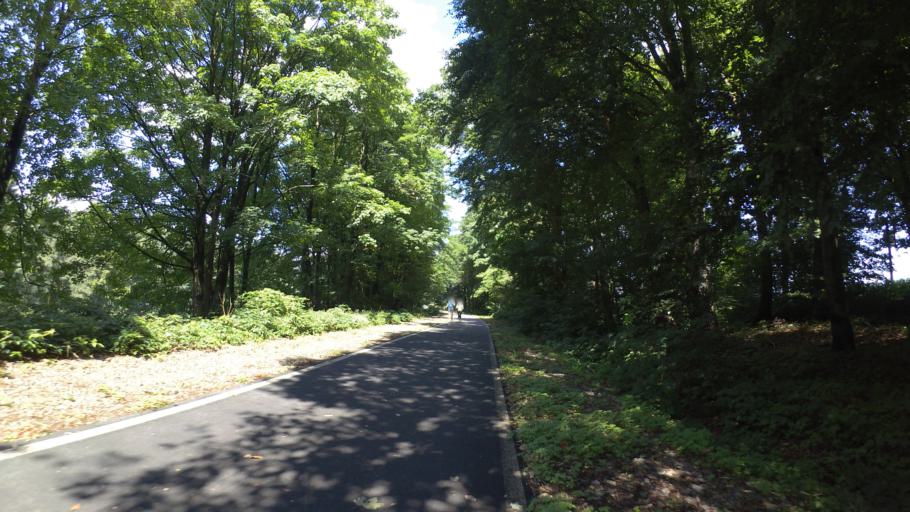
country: DE
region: North Rhine-Westphalia
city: Wermelskirchen
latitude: 51.1680
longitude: 7.2639
